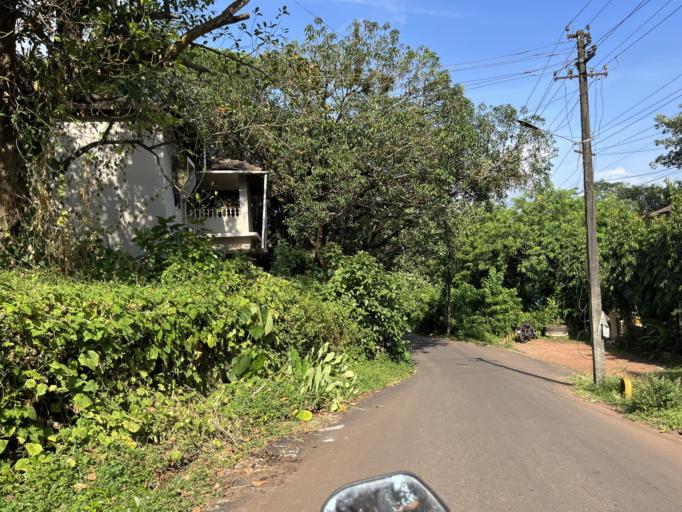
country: IN
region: Goa
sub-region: North Goa
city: Ponda
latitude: 15.3984
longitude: 74.0116
